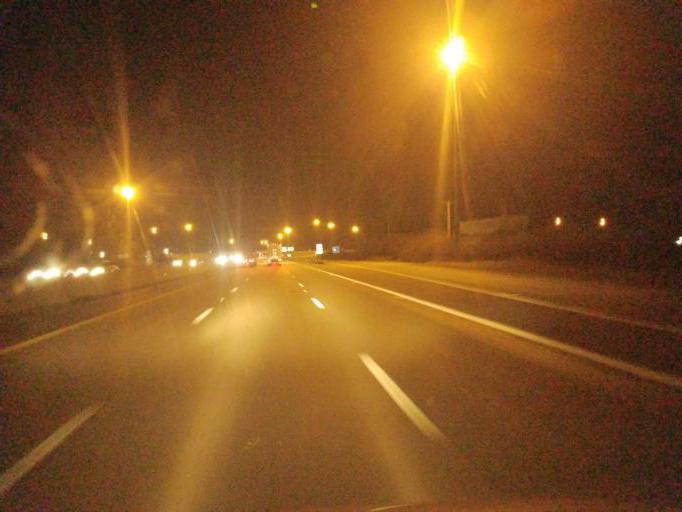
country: US
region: Ohio
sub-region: Clark County
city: Park Layne
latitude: 39.8655
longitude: -84.0640
